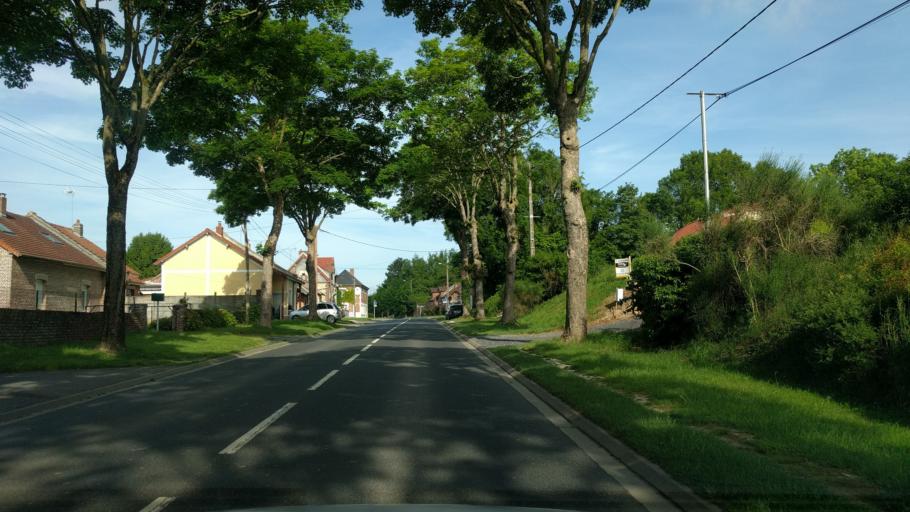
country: FR
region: Picardie
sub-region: Departement de la Somme
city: Peronne
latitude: 49.9580
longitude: 2.8901
